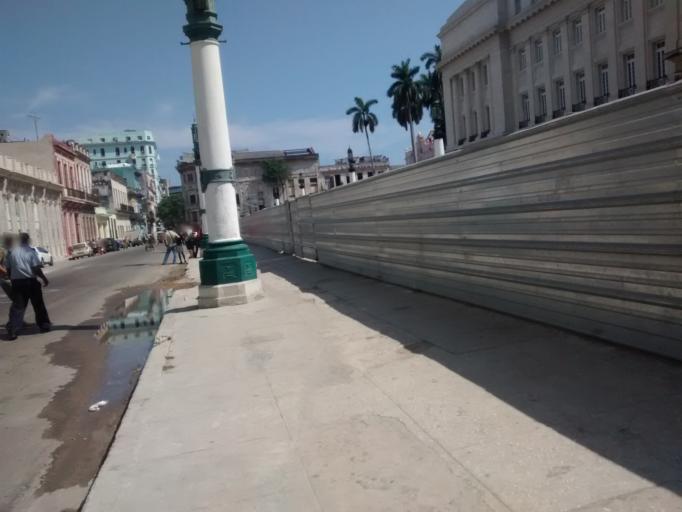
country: CU
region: La Habana
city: Centro Habana
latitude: 23.1349
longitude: -82.3603
